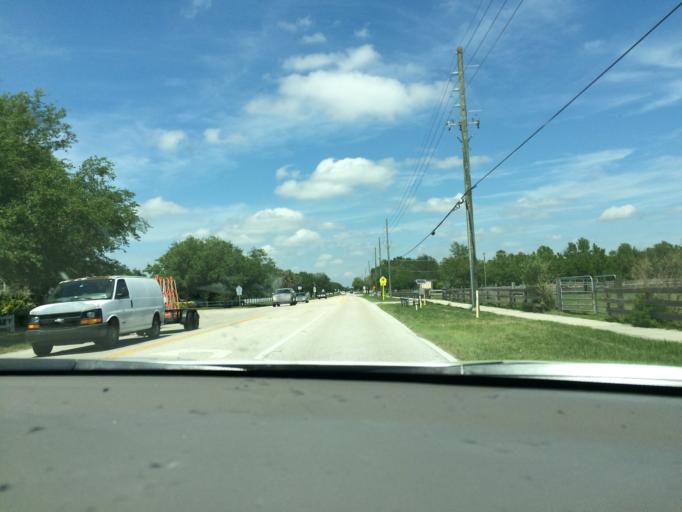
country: US
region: Florida
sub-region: Manatee County
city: Ellenton
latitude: 27.4933
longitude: -82.4337
